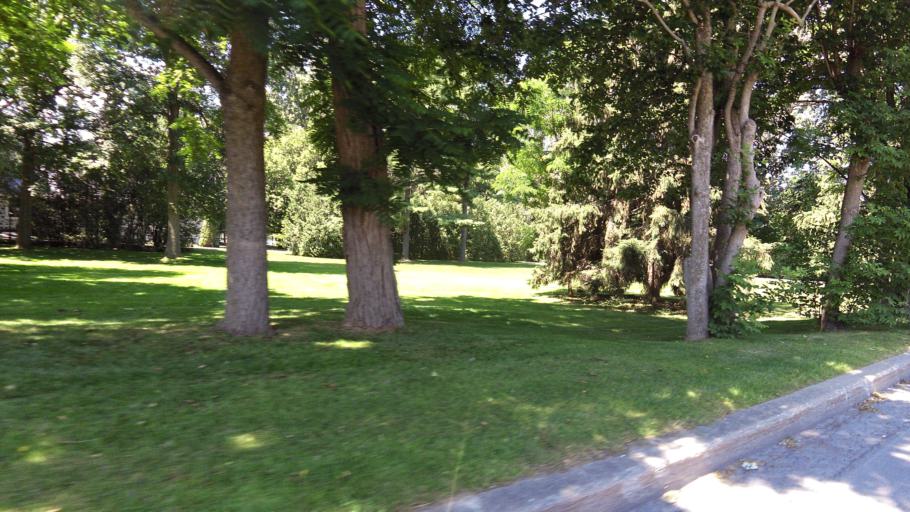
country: CA
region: Quebec
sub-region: Monteregie
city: Saint-Jean-sur-Richelieu
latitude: 45.3118
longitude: -73.2452
